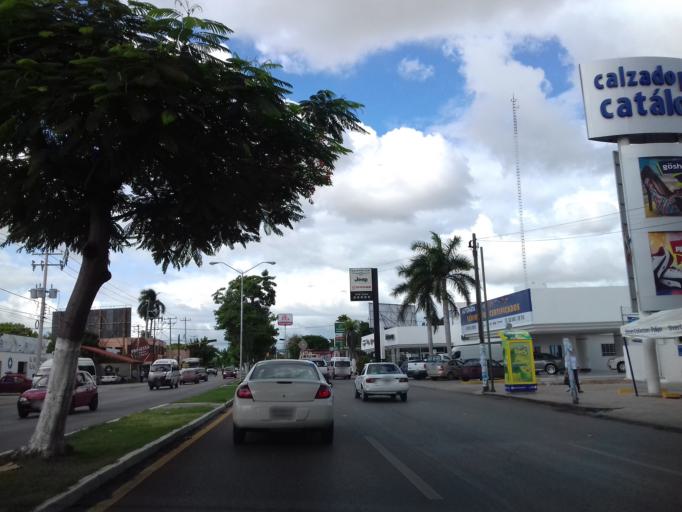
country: MX
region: Yucatan
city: Merida
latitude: 20.9583
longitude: -89.6423
